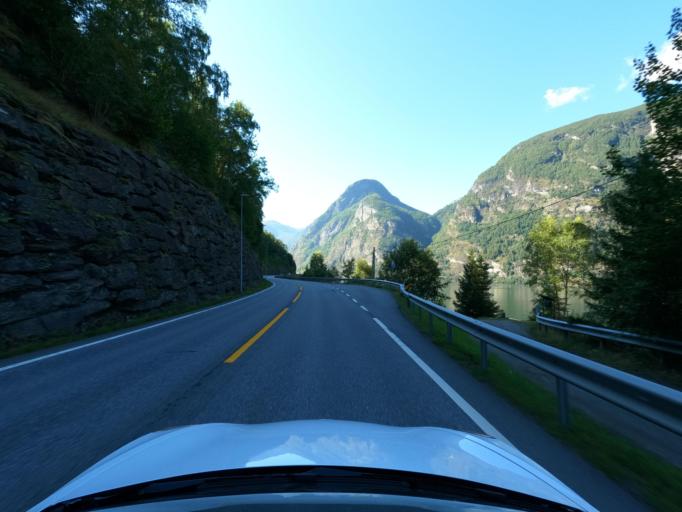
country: NO
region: Sogn og Fjordane
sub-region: Aurland
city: Aurlandsvangen
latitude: 60.8930
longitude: 7.1609
